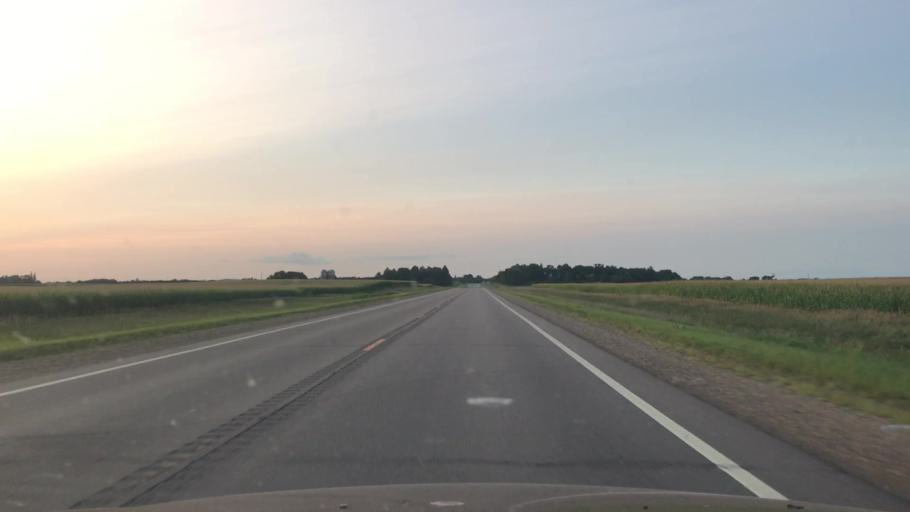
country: US
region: Minnesota
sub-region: Redwood County
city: Redwood Falls
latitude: 44.5110
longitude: -95.1180
